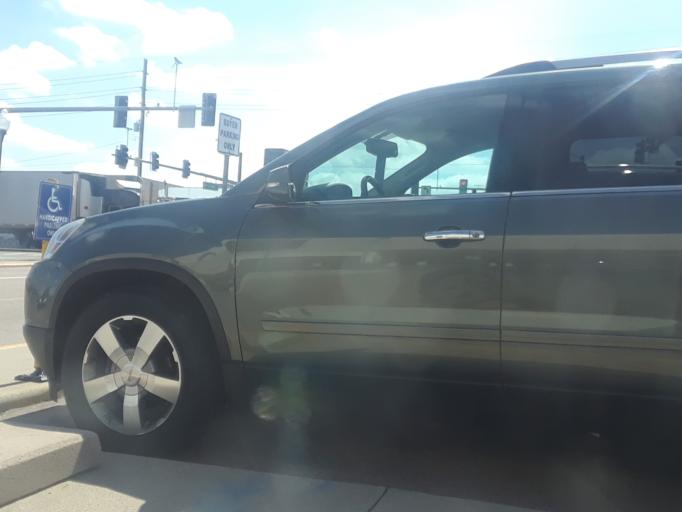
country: US
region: Colorado
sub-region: Adams County
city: Twin Lakes
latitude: 39.8023
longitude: -104.9815
